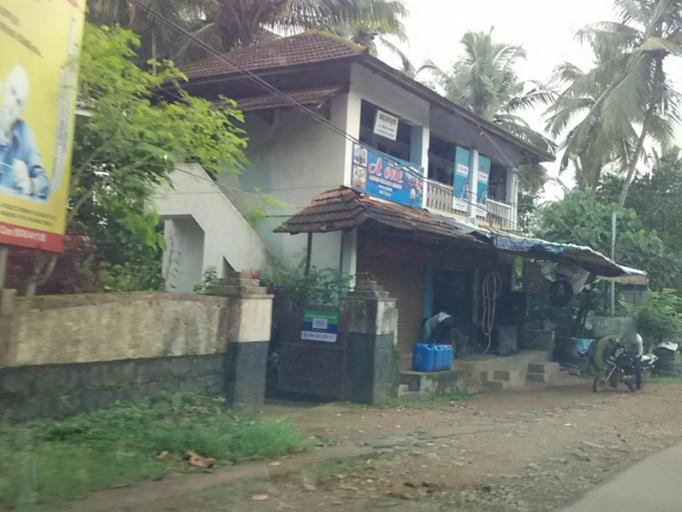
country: IN
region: Kerala
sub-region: Kozhikode
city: Kunnamangalam
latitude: 11.3068
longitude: 75.8945
